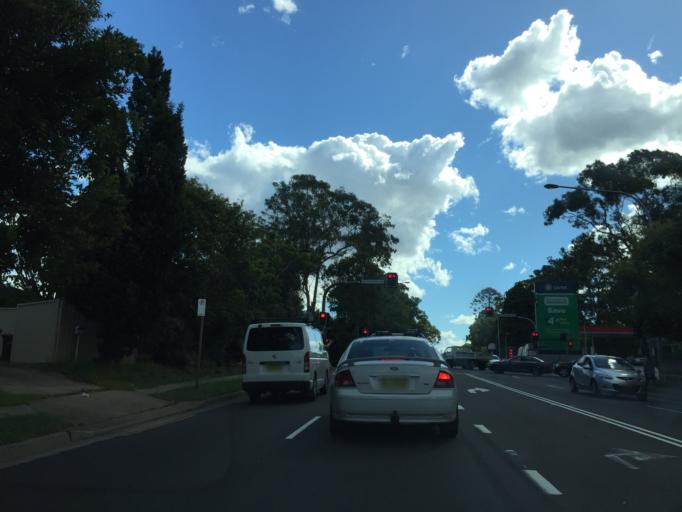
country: AU
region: New South Wales
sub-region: Parramatta
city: Telopea
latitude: -33.7875
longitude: 151.0290
